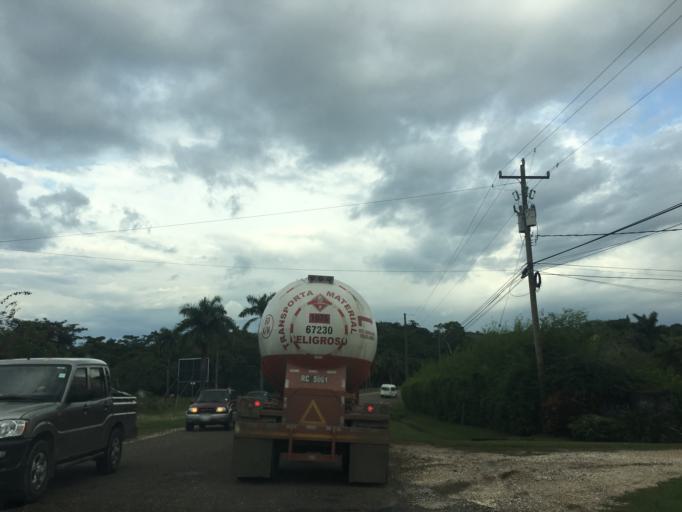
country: BZ
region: Cayo
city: San Ignacio
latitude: 17.2033
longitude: -88.9580
